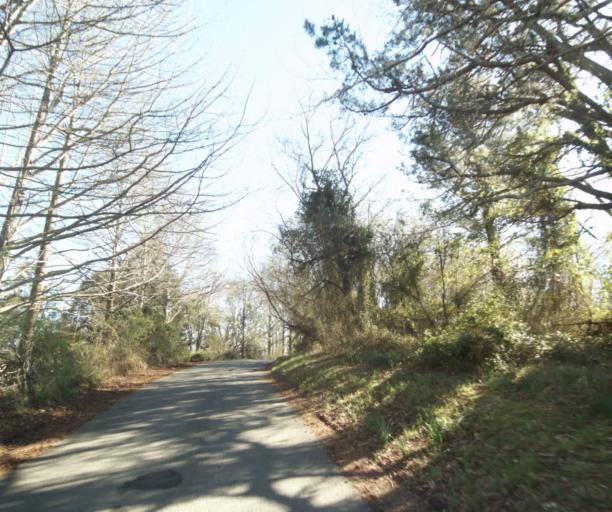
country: FR
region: Aquitaine
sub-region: Departement des Pyrenees-Atlantiques
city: Urrugne
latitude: 43.3634
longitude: -1.7351
